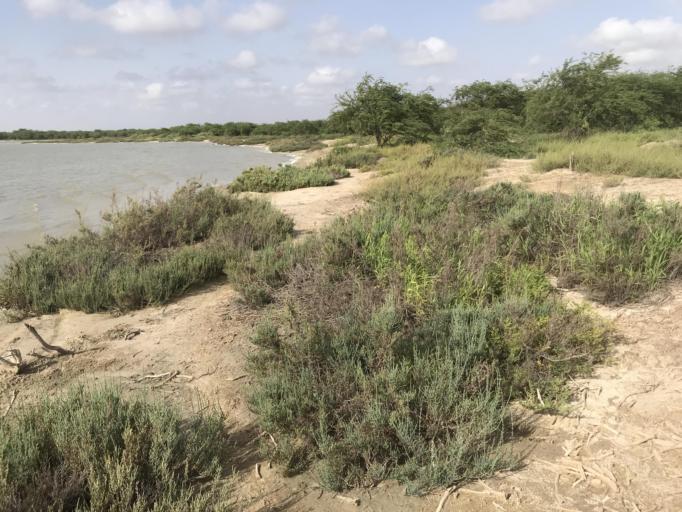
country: SN
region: Saint-Louis
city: Saint-Louis
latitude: 15.9257
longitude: -16.4563
